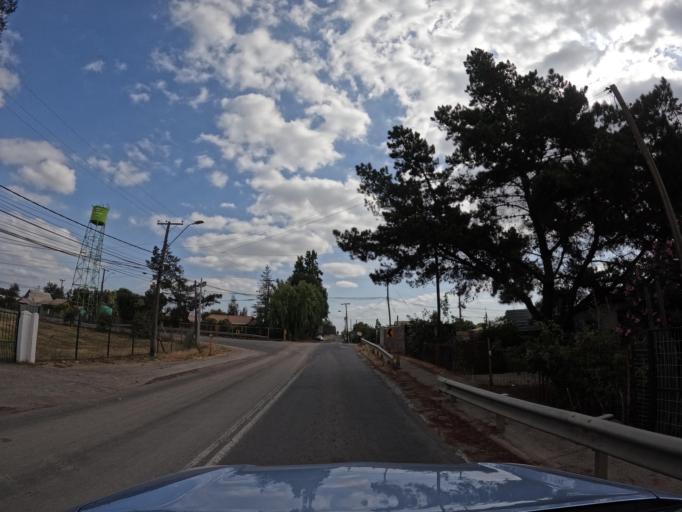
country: CL
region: Maule
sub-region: Provincia de Curico
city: Molina
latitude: -35.1619
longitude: -71.2872
